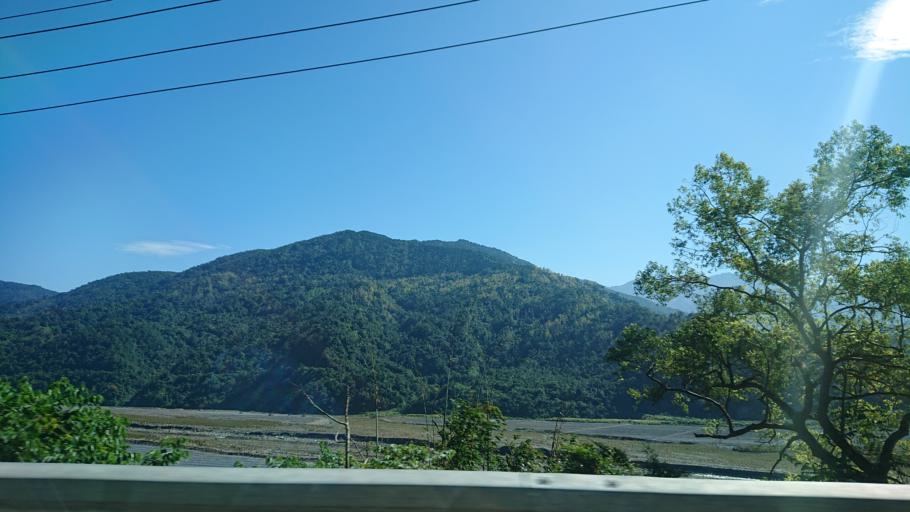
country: TW
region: Taiwan
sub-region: Yilan
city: Yilan
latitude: 24.5818
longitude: 121.4968
